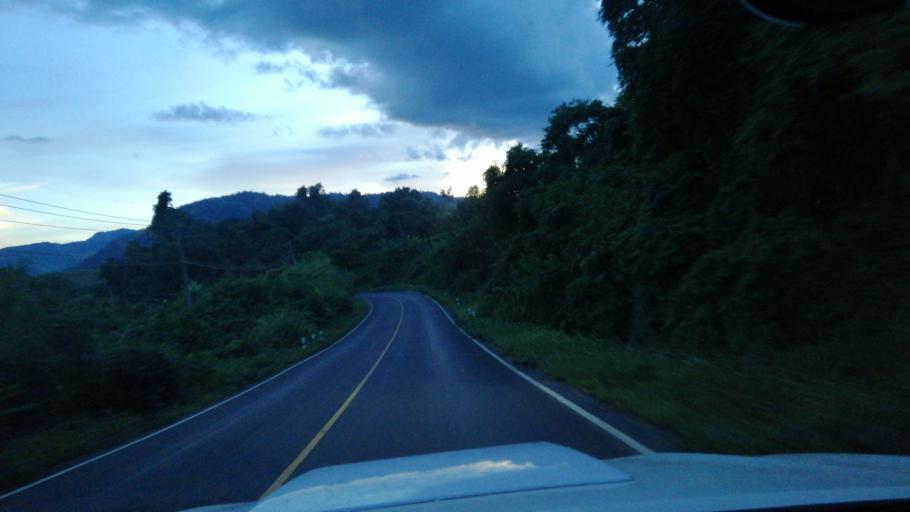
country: TH
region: Phayao
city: Phu Sang
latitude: 19.7650
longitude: 100.5759
